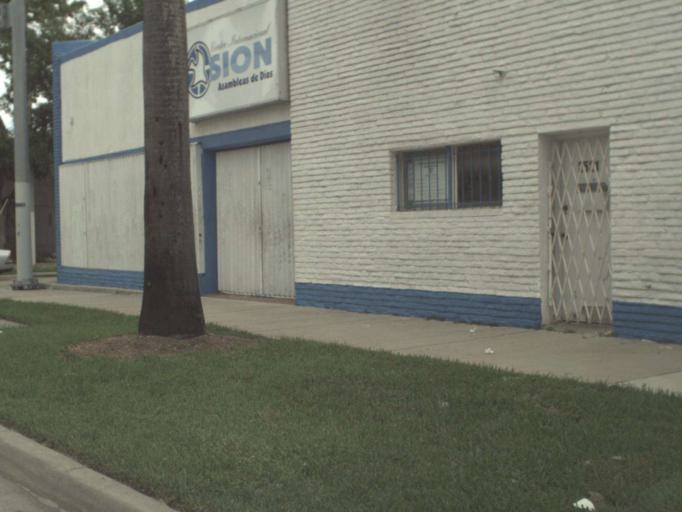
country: US
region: Florida
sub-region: Miami-Dade County
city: Miami
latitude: 25.8014
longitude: -80.1891
